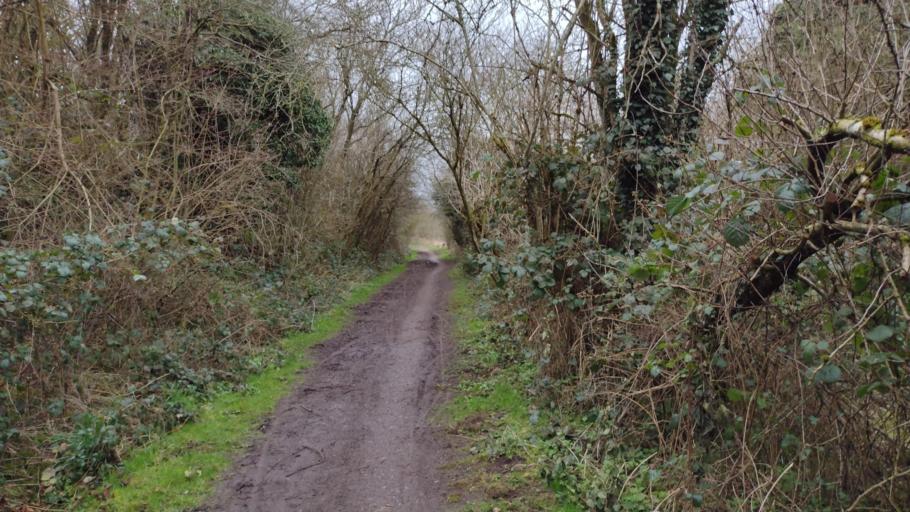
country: GB
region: England
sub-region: Wiltshire
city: Marlborough
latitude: 51.4338
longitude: -1.7271
